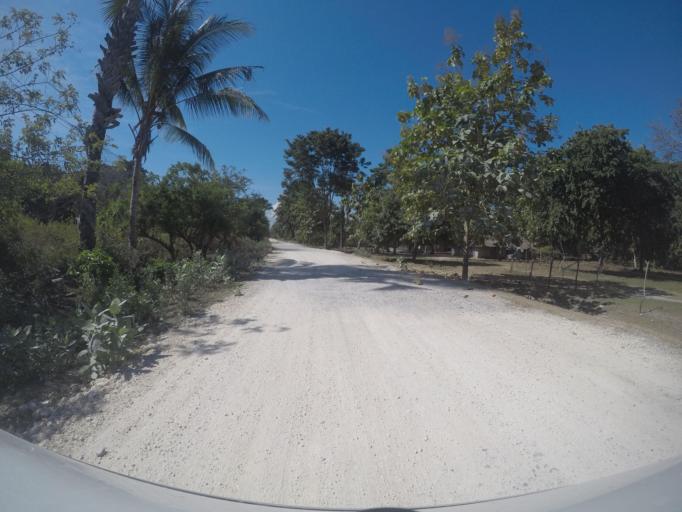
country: TL
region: Viqueque
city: Viqueque
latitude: -8.9077
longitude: 126.5049
